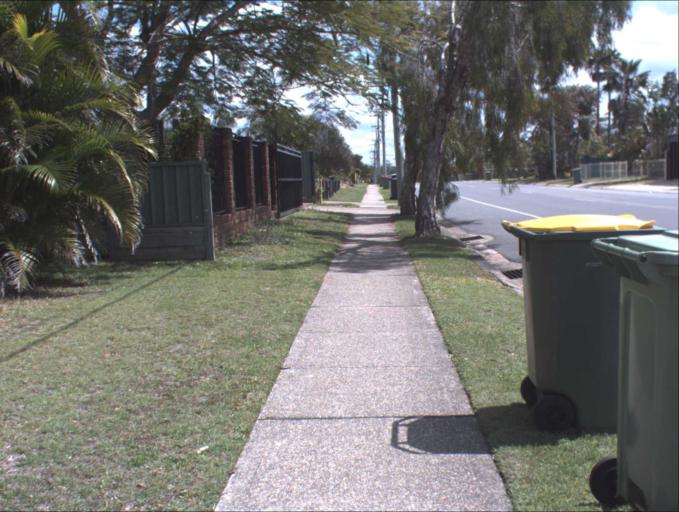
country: AU
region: Queensland
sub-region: Logan
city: Waterford West
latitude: -27.6825
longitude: 153.1497
